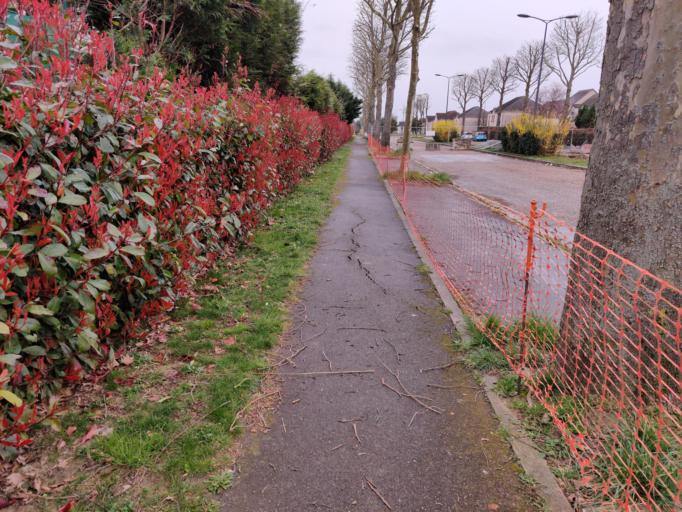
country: FR
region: Ile-de-France
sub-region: Departement du Val-d'Oise
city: Fontenay-en-Parisis
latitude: 49.0302
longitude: 2.4484
